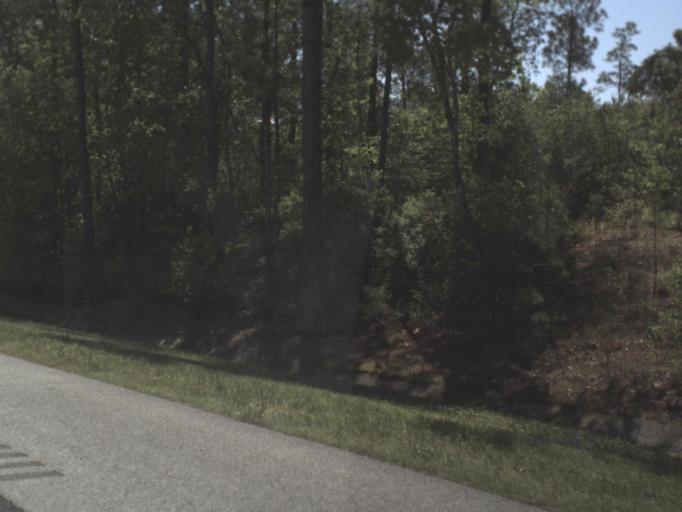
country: US
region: Florida
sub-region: Escambia County
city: Cantonment
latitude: 30.5640
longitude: -87.3817
